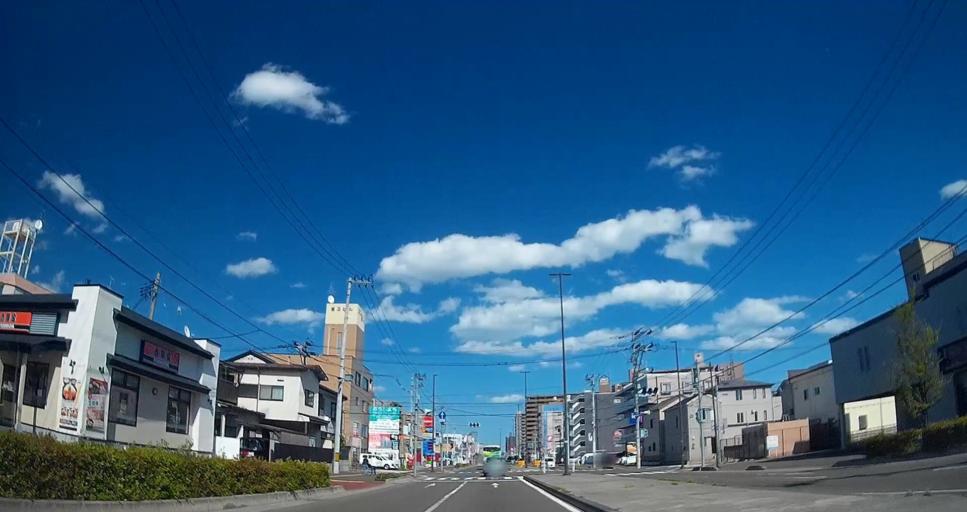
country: JP
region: Miyagi
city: Sendai-shi
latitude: 38.2519
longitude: 140.9123
